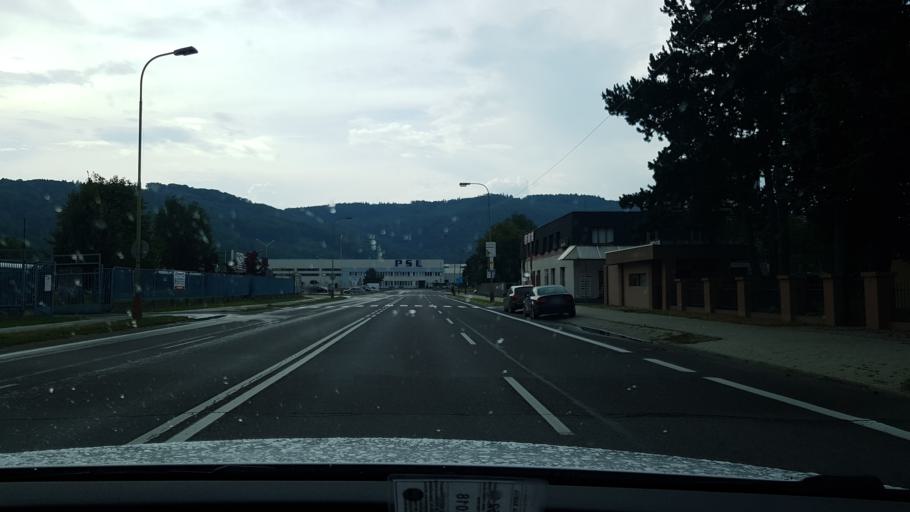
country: SK
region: Trenciansky
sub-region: Okres Povazska Bystrica
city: Povazska Bystrica
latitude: 49.1188
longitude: 18.4276
